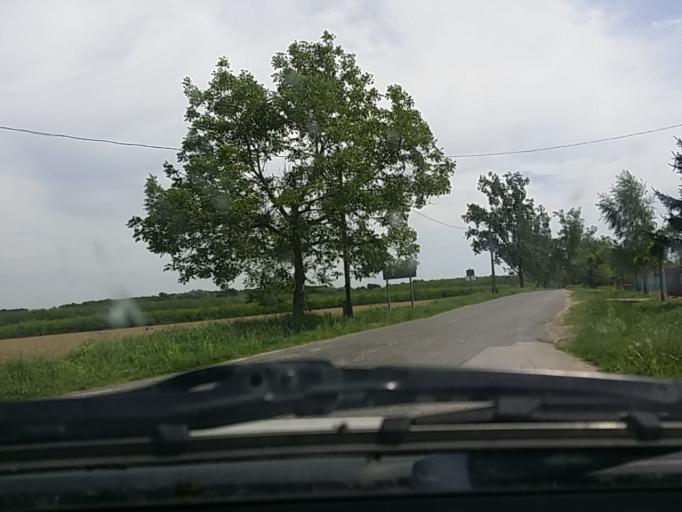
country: HU
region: Somogy
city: Barcs
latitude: 45.9535
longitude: 17.6203
